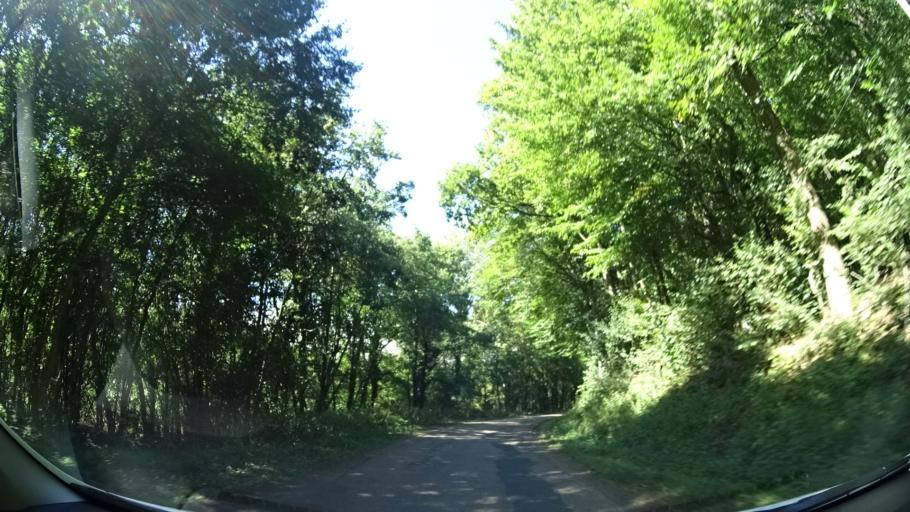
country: FR
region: Centre
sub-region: Departement du Loiret
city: Trigueres
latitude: 47.9454
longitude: 2.9853
